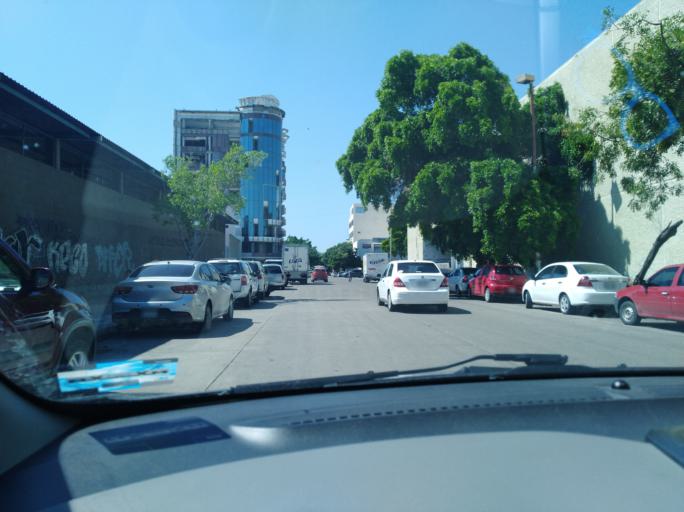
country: MX
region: Sinaloa
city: Culiacan
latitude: 24.7942
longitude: -107.4116
